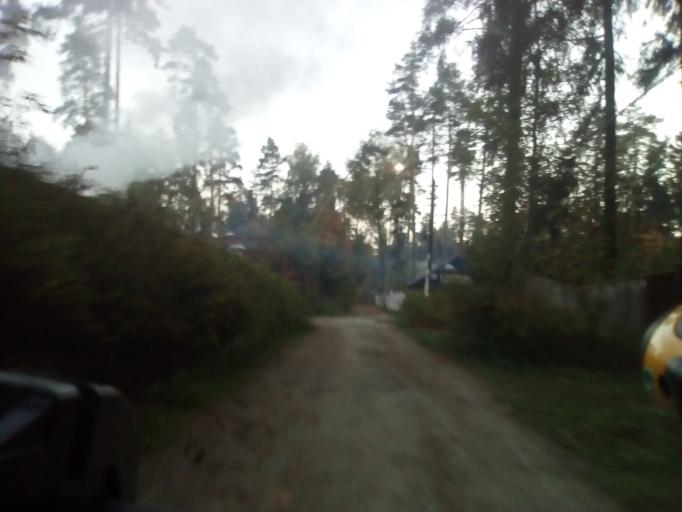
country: RU
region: Moskovskaya
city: Kratovo
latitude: 55.5998
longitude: 38.1582
